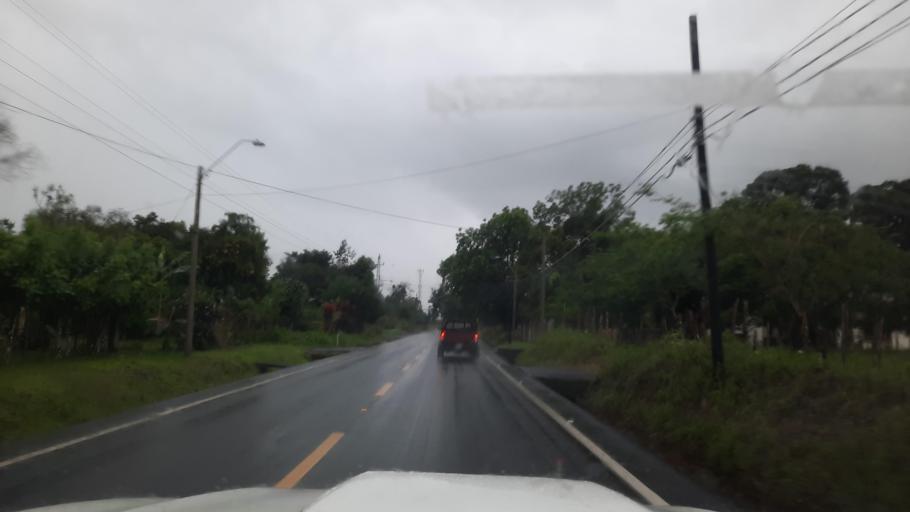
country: PA
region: Chiriqui
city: Sortova
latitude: 8.5587
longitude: -82.6276
